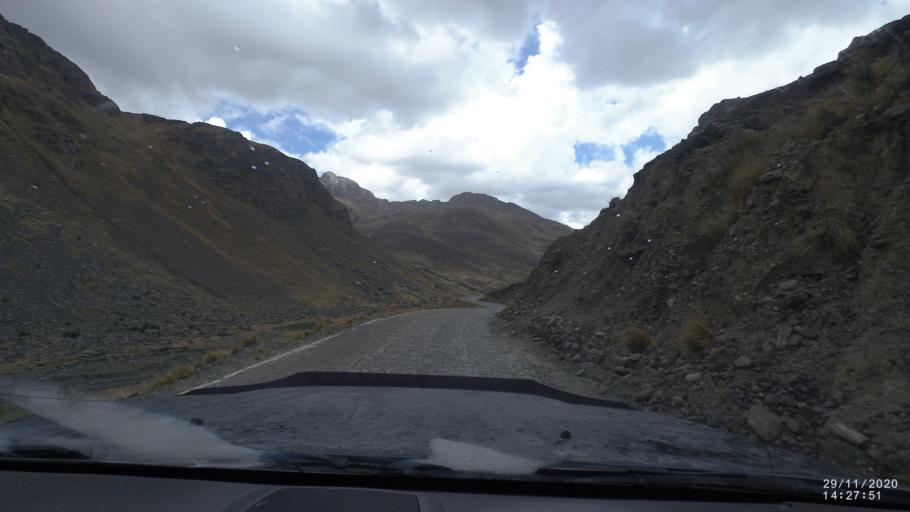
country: BO
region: Cochabamba
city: Sipe Sipe
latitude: -17.2589
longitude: -66.3639
